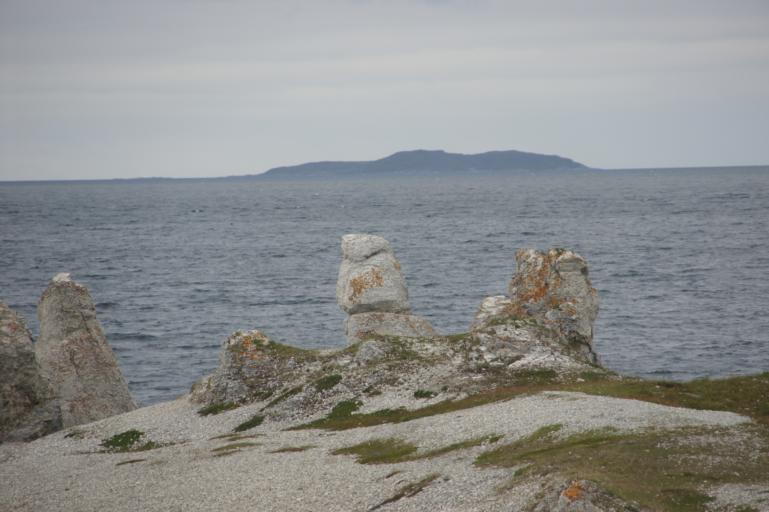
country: NO
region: Finnmark Fylke
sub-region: Porsanger
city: Lakselv
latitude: 70.3056
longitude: 25.1779
